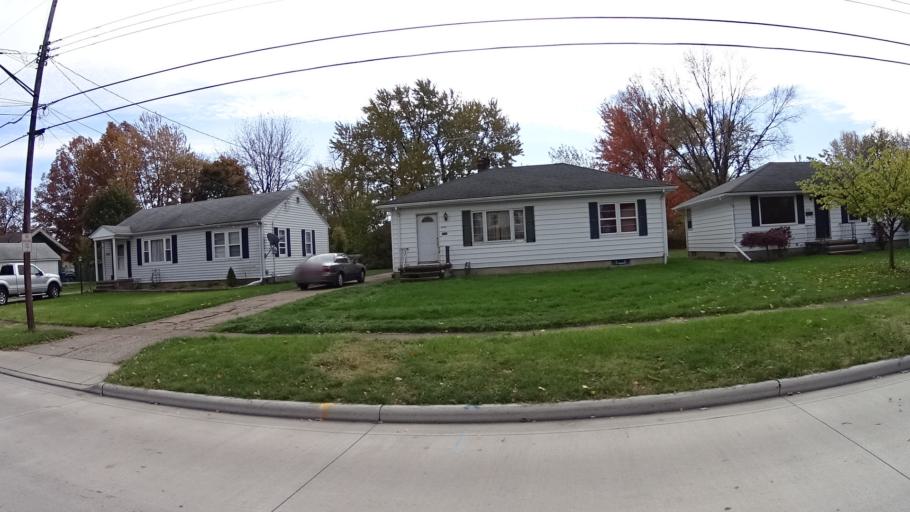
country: US
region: Ohio
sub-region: Lorain County
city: Sheffield Lake
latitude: 41.4792
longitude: -82.1329
